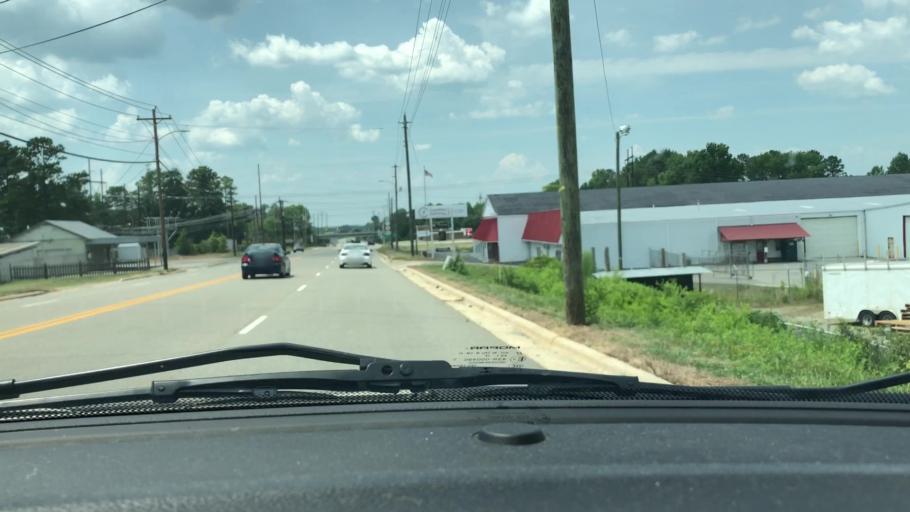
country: US
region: North Carolina
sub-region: Lee County
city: Sanford
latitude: 35.4925
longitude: -79.1914
